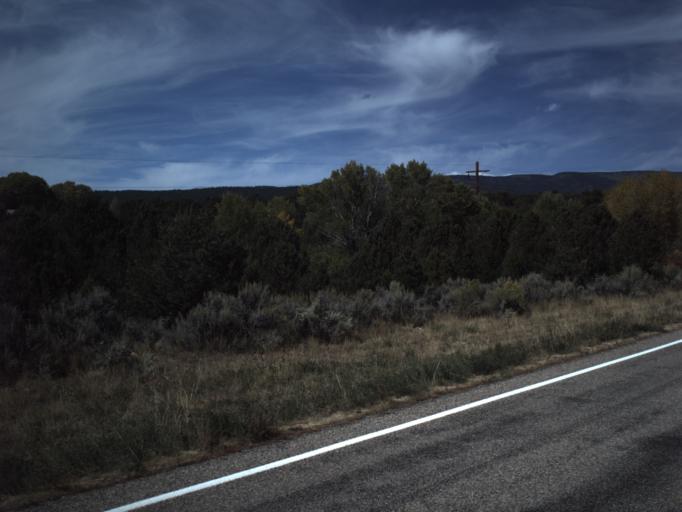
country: US
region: Utah
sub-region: Wayne County
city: Loa
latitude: 37.9483
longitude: -111.4330
